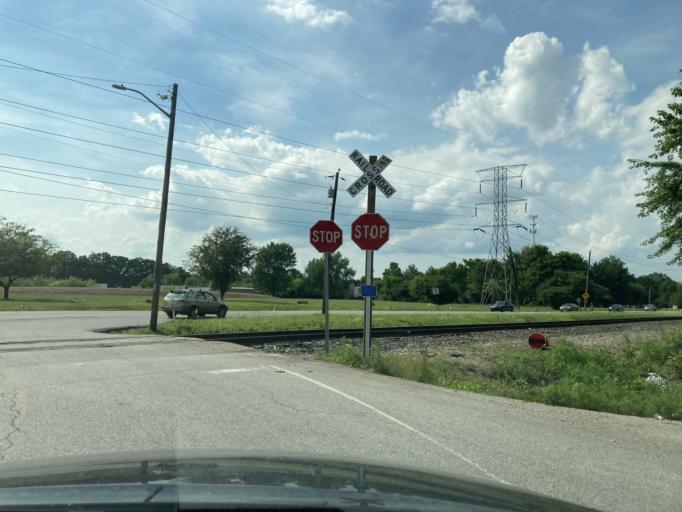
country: US
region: Indiana
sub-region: Marion County
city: Speedway
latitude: 39.8314
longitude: -86.2260
